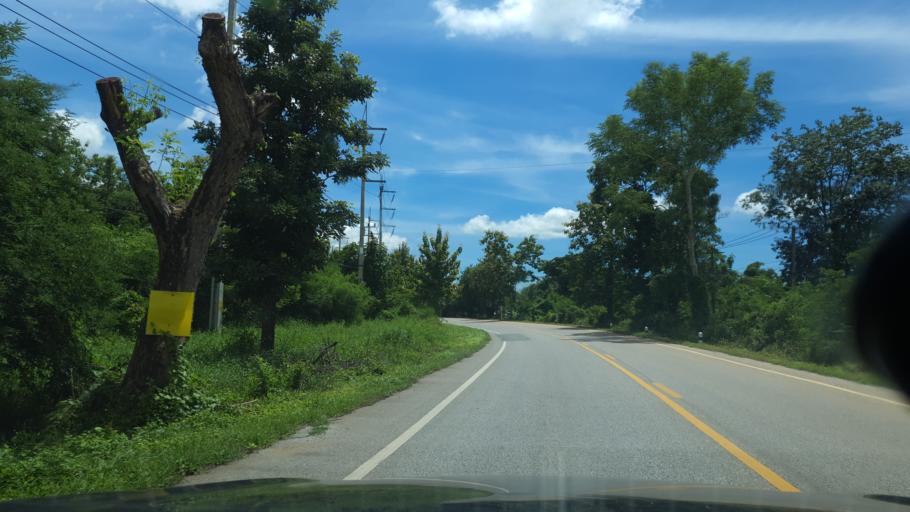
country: TH
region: Sukhothai
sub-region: Amphoe Si Satchanalai
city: Si Satchanalai
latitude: 17.4811
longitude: 99.7622
